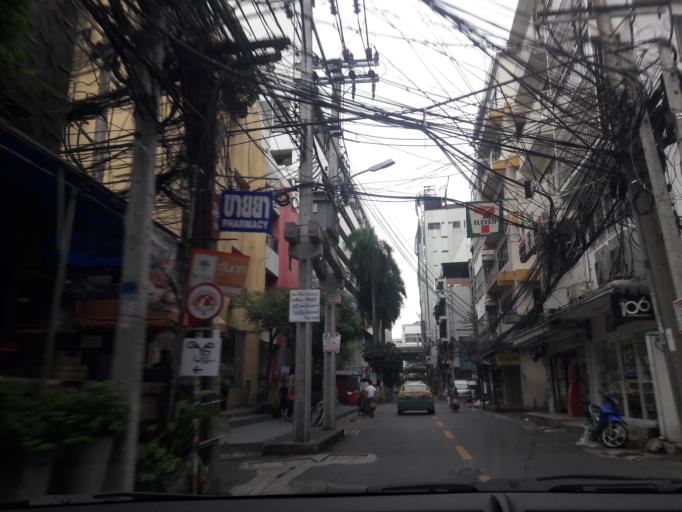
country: TH
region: Bangkok
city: Bang Rak
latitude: 13.7258
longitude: 100.5313
